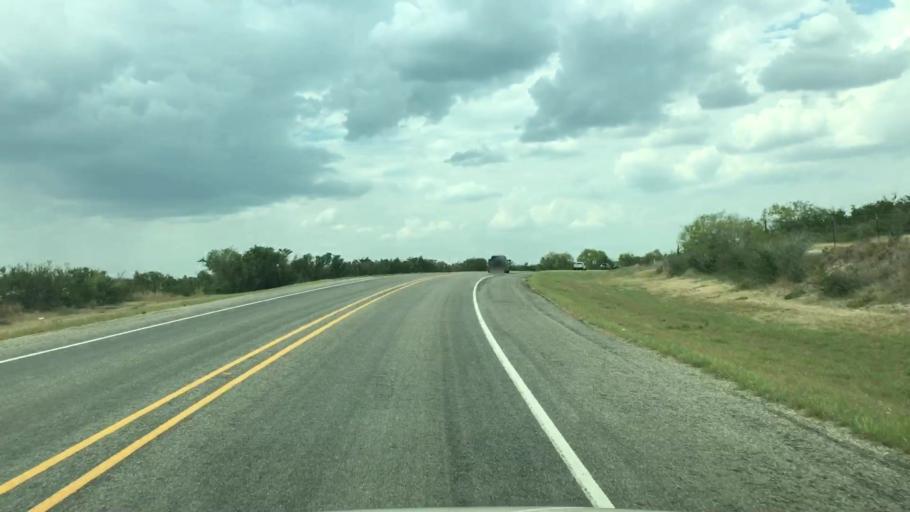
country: US
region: Texas
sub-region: Live Oak County
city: Three Rivers
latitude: 28.6411
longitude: -98.2826
